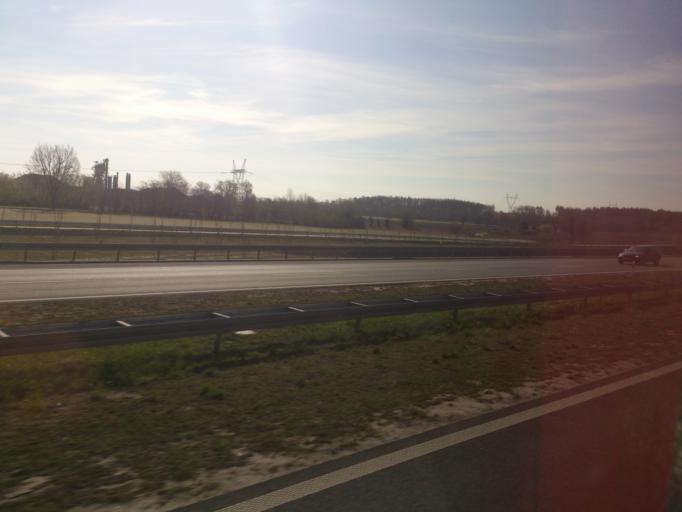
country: PL
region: Kujawsko-Pomorskie
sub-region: Powiat aleksandrowski
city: Waganiec
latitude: 52.7849
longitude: 18.8424
